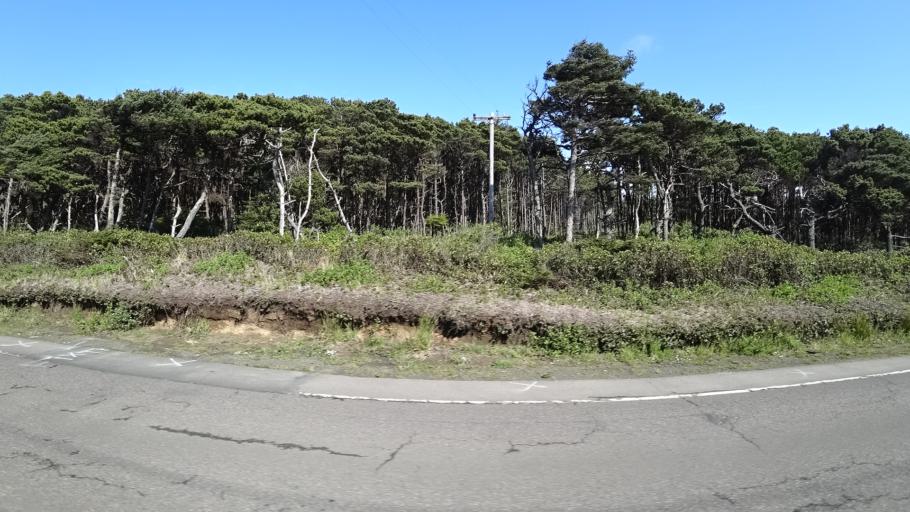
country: US
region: Oregon
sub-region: Lincoln County
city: Newport
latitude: 44.5588
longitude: -124.0708
